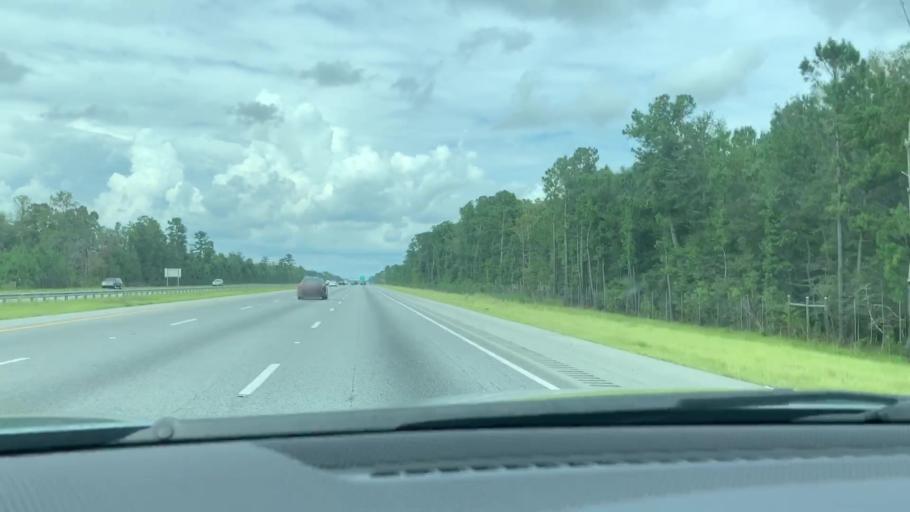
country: US
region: Georgia
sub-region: McIntosh County
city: Darien
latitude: 31.5045
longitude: -81.4462
